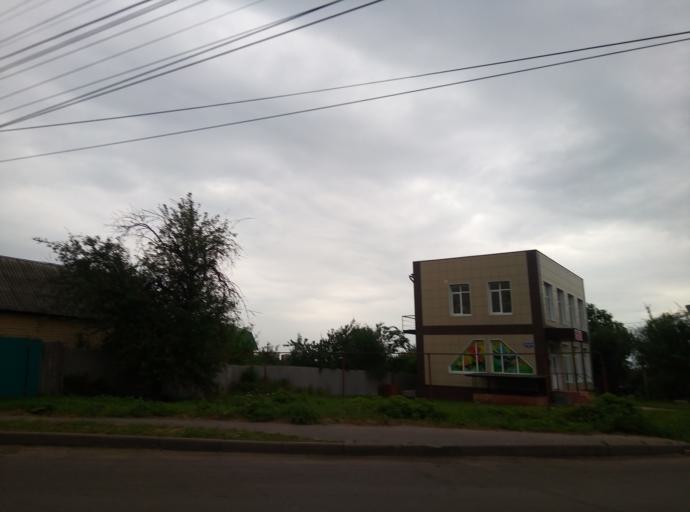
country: RU
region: Kursk
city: Kursk
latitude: 51.7428
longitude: 36.1527
